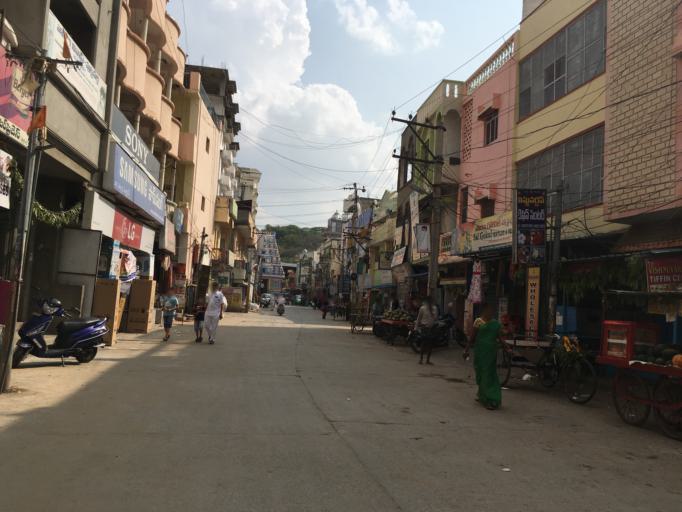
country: IN
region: Andhra Pradesh
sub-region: Anantapur
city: Puttaparthi
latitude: 14.1678
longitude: 77.8112
